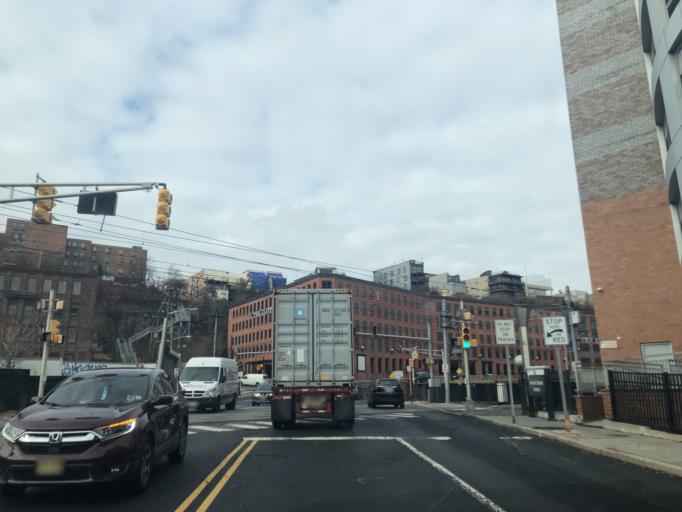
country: US
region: New Jersey
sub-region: Hudson County
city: Hoboken
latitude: 40.7396
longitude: -74.0431
